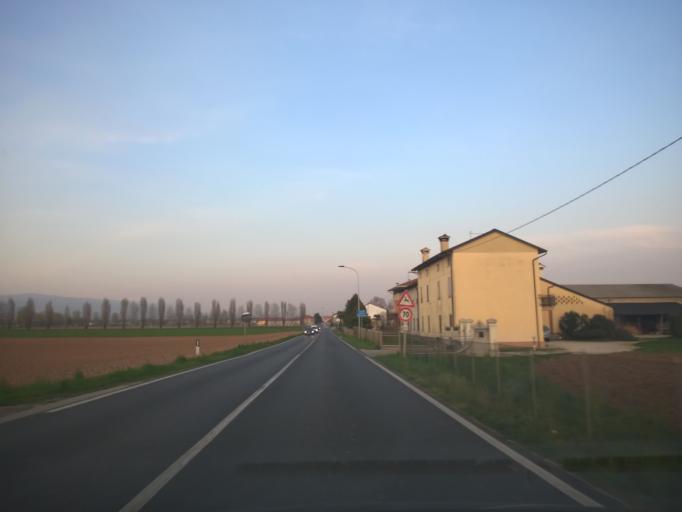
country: IT
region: Veneto
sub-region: Provincia di Vicenza
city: Malo
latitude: 45.6665
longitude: 11.4487
